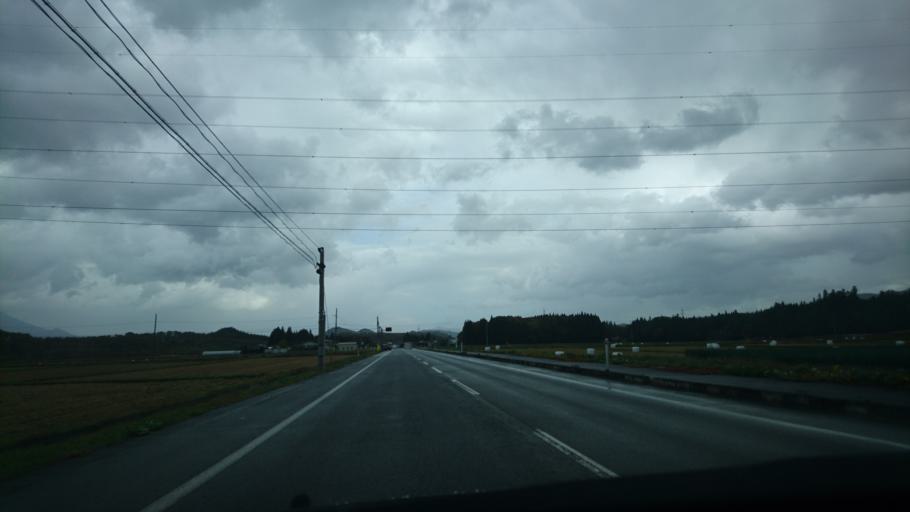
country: JP
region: Iwate
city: Shizukuishi
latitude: 39.6558
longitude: 140.9584
